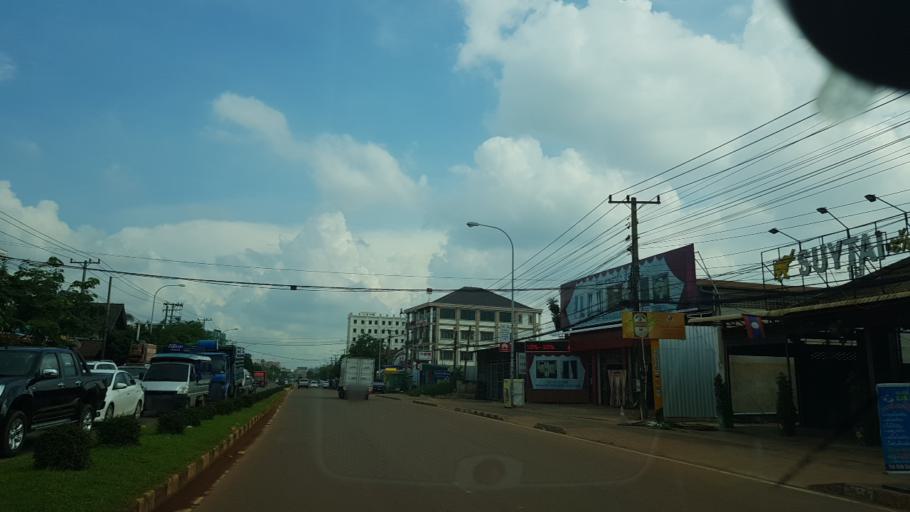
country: LA
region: Vientiane
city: Vientiane
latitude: 18.0300
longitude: 102.6517
